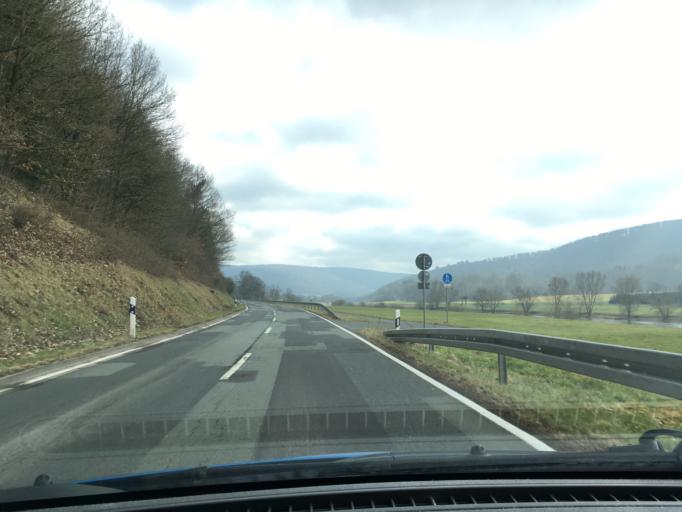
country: DE
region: Lower Saxony
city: Bodenfelde
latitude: 51.5638
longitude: 9.6046
